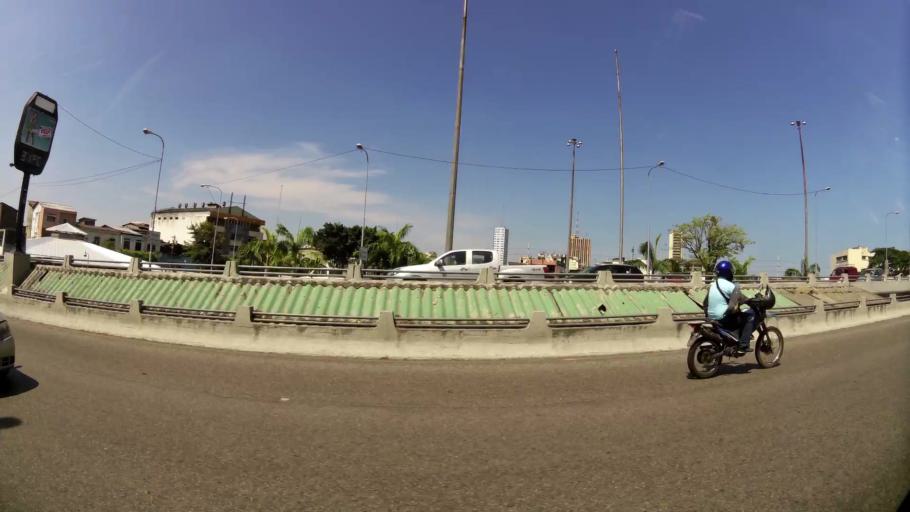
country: EC
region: Guayas
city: Guayaquil
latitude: -2.1835
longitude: -79.8874
